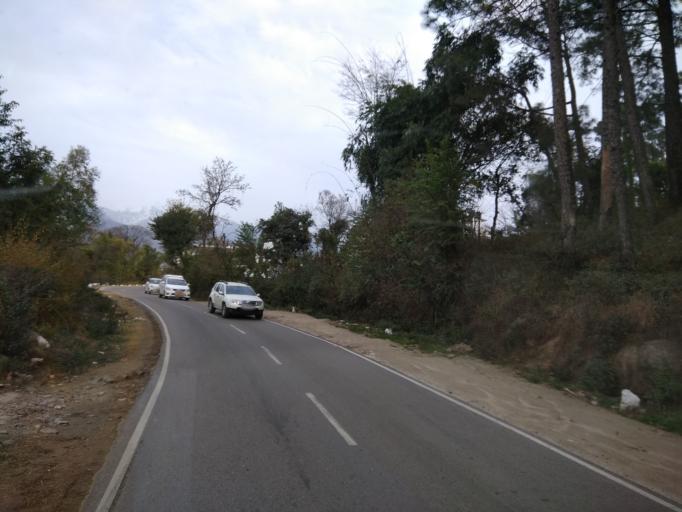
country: IN
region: Himachal Pradesh
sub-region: Kangra
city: Palampur
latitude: 32.1146
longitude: 76.5120
